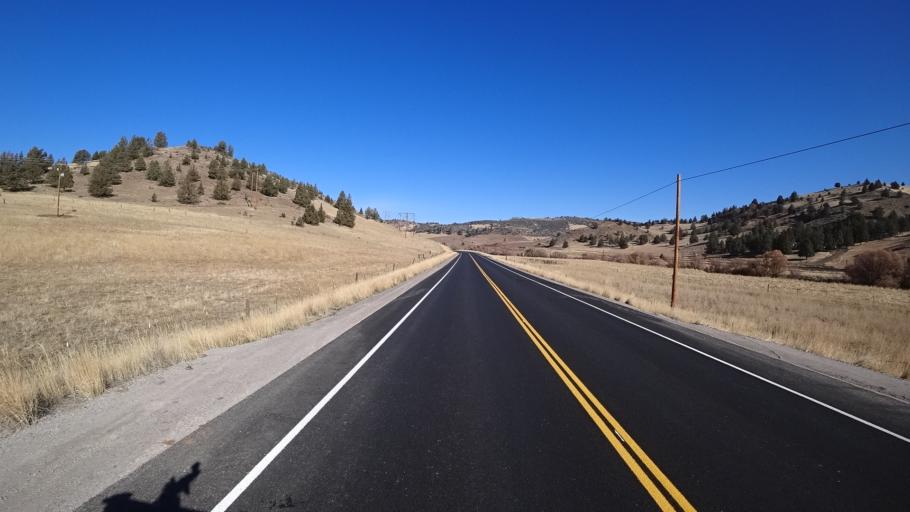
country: US
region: California
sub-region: Siskiyou County
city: Montague
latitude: 41.8589
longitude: -122.4646
